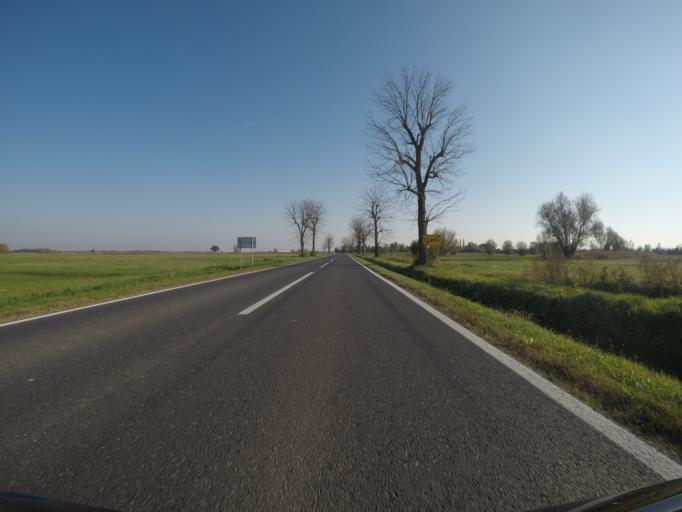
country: HR
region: Koprivnicko-Krizevacka
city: Kalinovac
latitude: 46.0254
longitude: 17.0772
